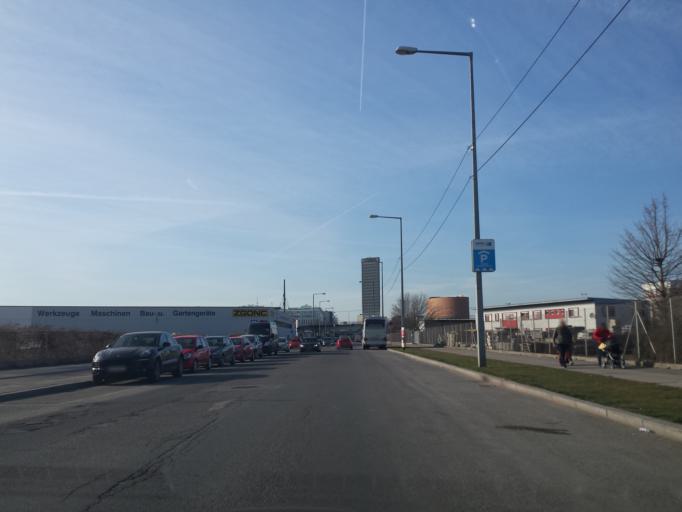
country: AT
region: Vienna
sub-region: Wien Stadt
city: Vienna
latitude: 48.1873
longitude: 16.4203
